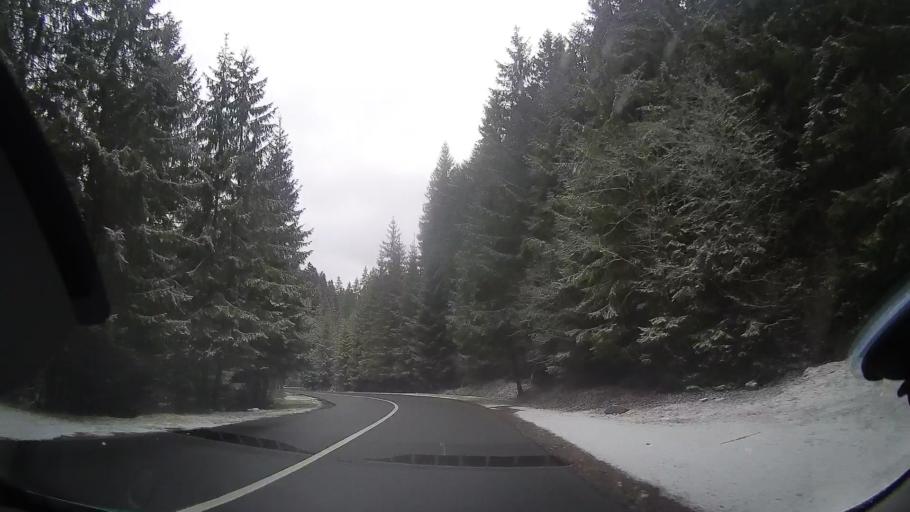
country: RO
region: Cluj
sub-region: Comuna Calatele
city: Calatele
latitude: 46.7330
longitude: 23.0401
